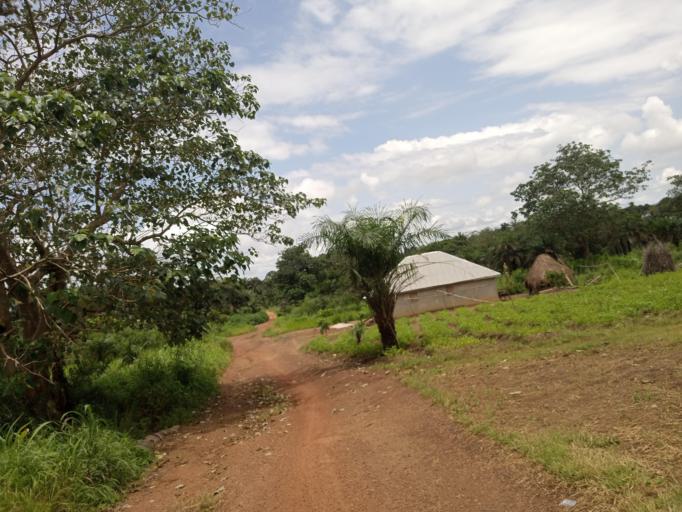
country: SL
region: Northern Province
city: Kamakwie
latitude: 9.4873
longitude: -12.2439
